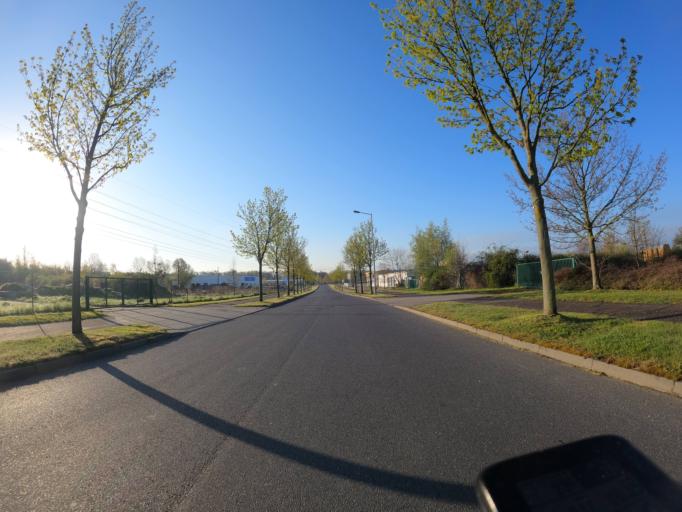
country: DE
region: Brandenburg
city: Neuenhagen
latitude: 52.5327
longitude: 13.7133
